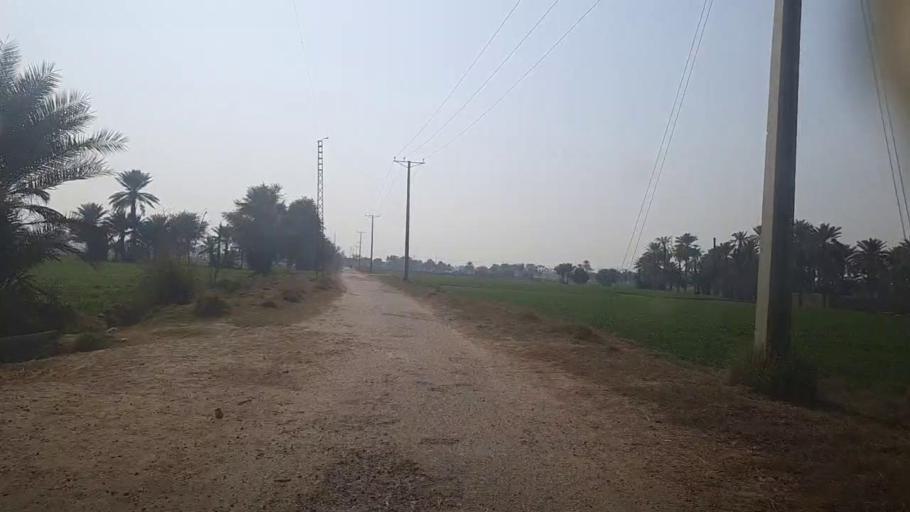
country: PK
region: Sindh
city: Kot Diji
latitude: 27.3491
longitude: 68.7324
